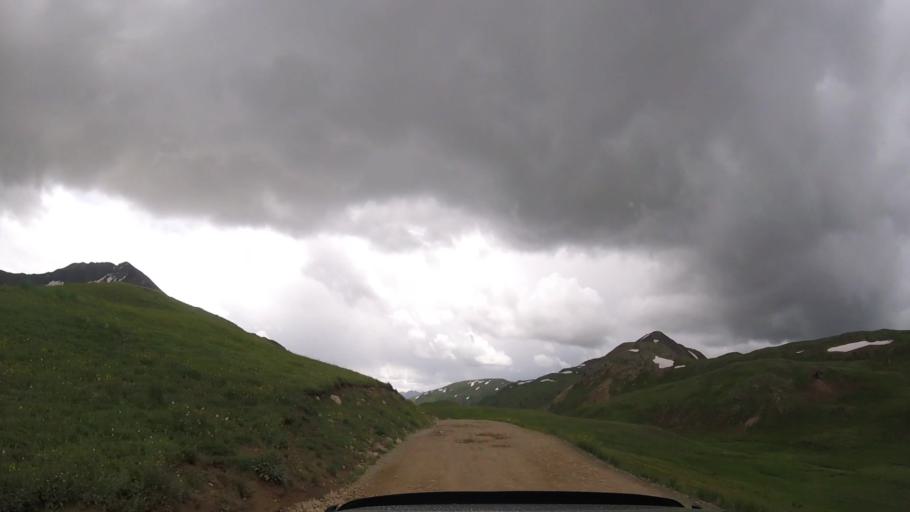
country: US
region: Colorado
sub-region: Ouray County
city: Ouray
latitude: 37.9560
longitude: -107.5751
